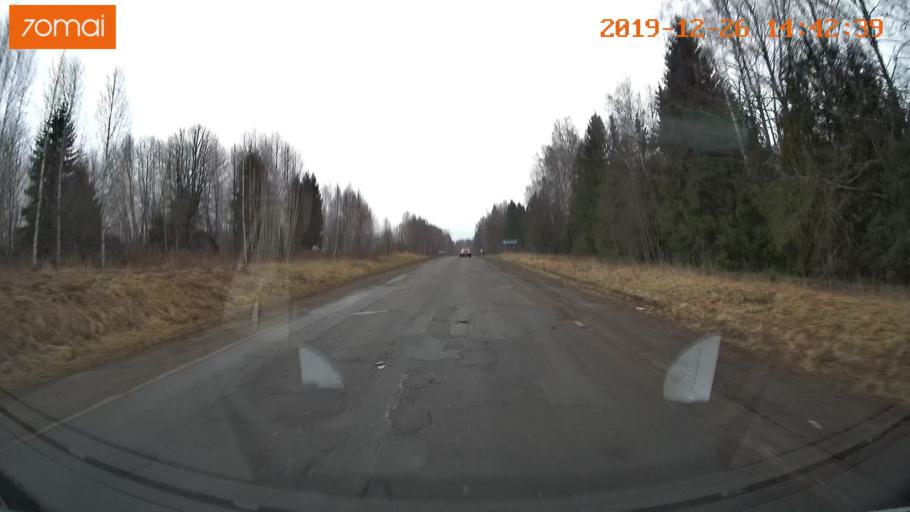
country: RU
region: Jaroslavl
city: Poshekhon'ye
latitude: 58.3625
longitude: 39.0326
